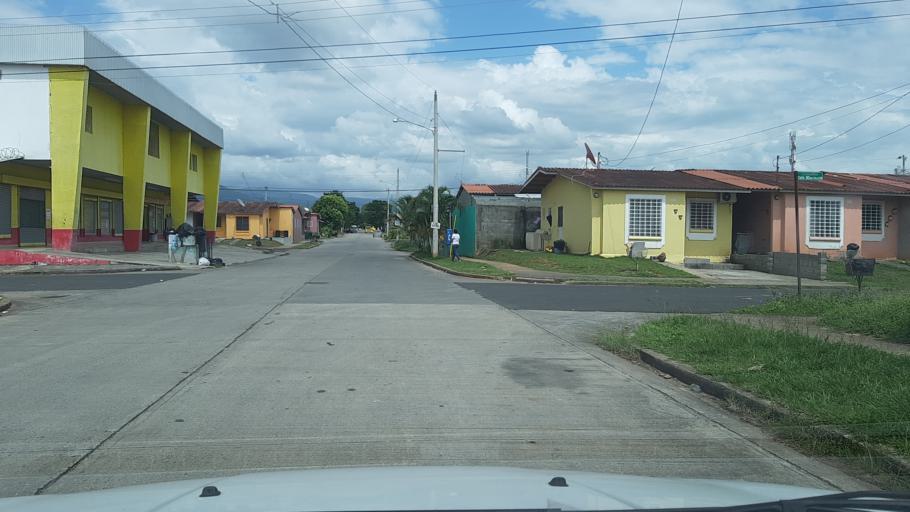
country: PA
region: Panama
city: Tocumen
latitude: 9.0704
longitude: -79.3617
